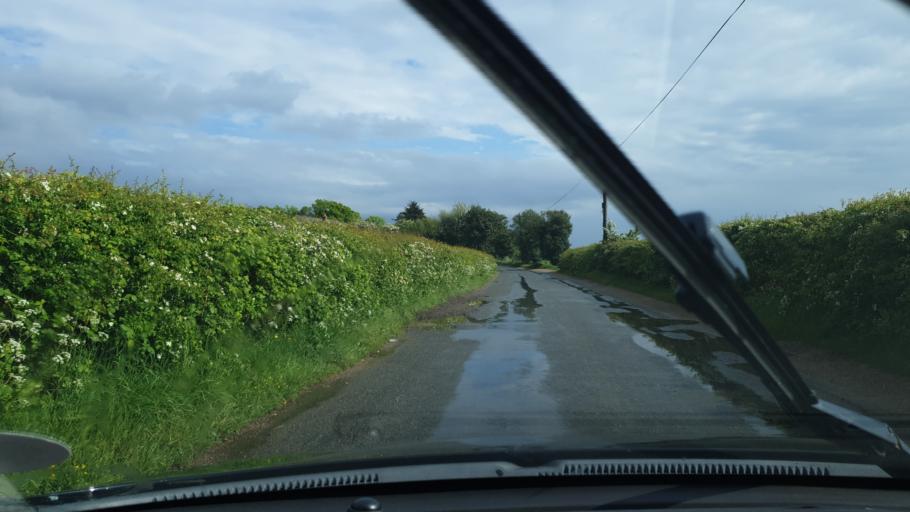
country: GB
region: England
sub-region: Essex
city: Great Bentley
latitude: 51.8473
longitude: 1.0466
